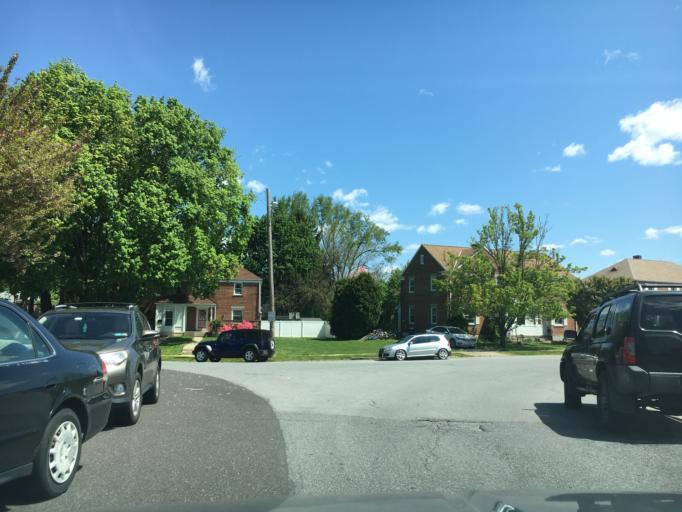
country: US
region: Pennsylvania
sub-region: Lehigh County
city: Allentown
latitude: 40.5802
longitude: -75.4821
